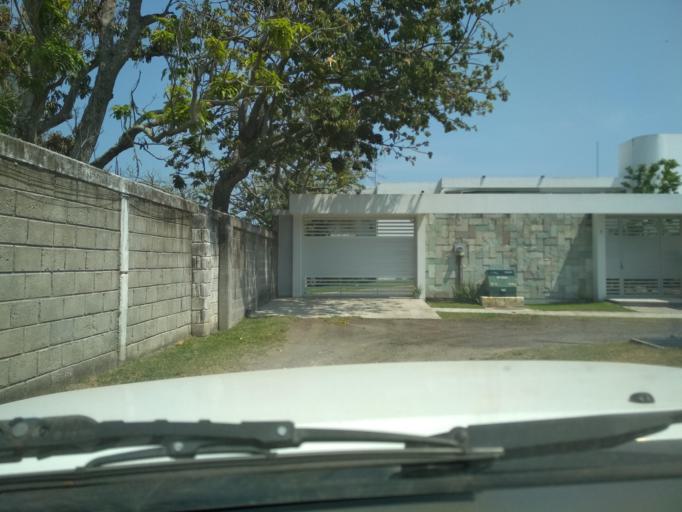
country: MX
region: Veracruz
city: Boca del Rio
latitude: 19.0948
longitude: -96.1170
